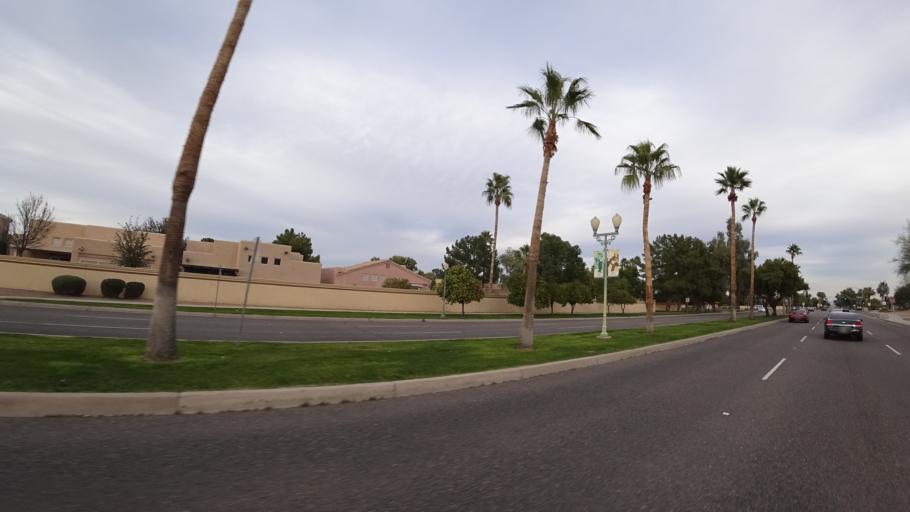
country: US
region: Arizona
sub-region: Maricopa County
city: Sun City West
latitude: 33.6386
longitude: -112.3702
